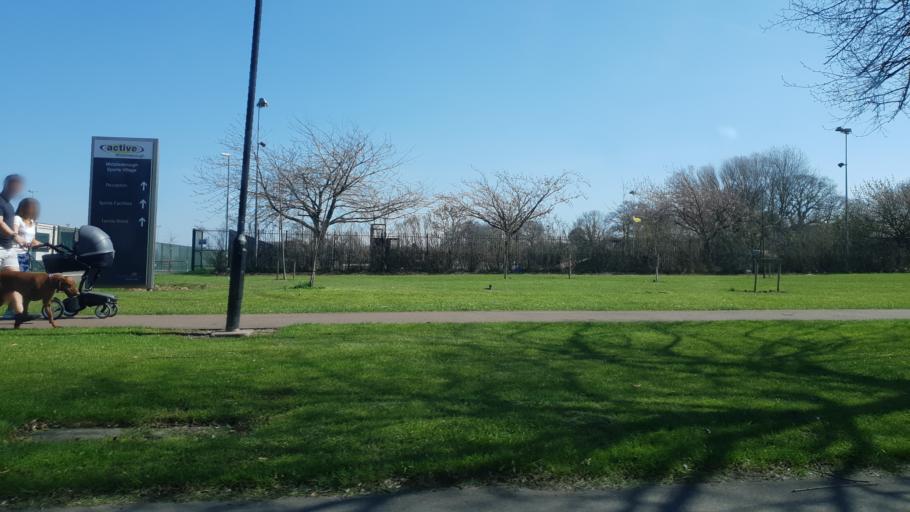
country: GB
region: England
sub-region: Middlesbrough
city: Nunthorpe
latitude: 54.5428
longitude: -1.2124
